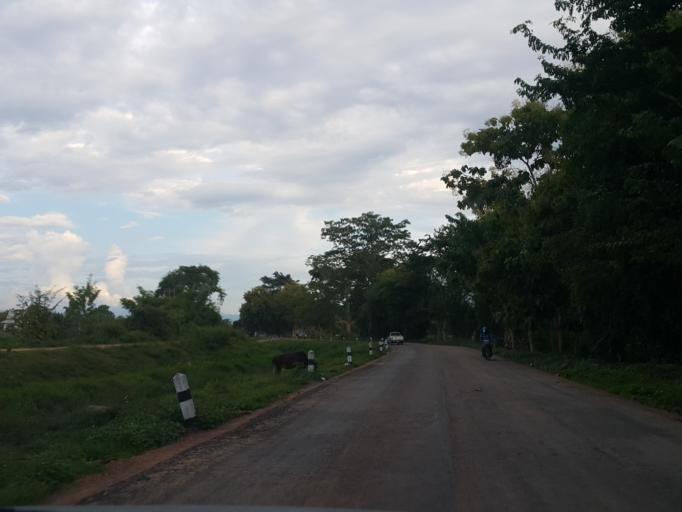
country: TH
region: Chiang Mai
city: San Sai
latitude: 18.8968
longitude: 99.0539
